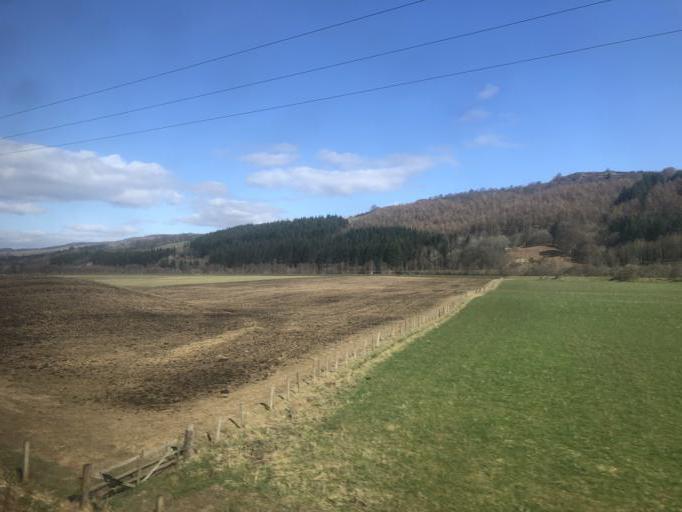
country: GB
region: Scotland
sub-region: Perth and Kinross
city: Pitlochry
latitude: 56.5889
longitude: -3.6295
